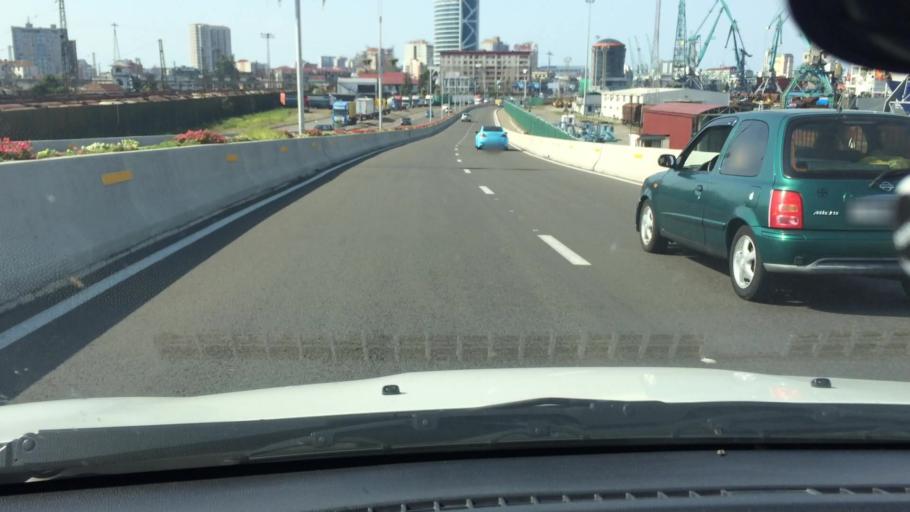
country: GE
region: Ajaria
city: Batumi
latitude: 41.6463
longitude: 41.6574
